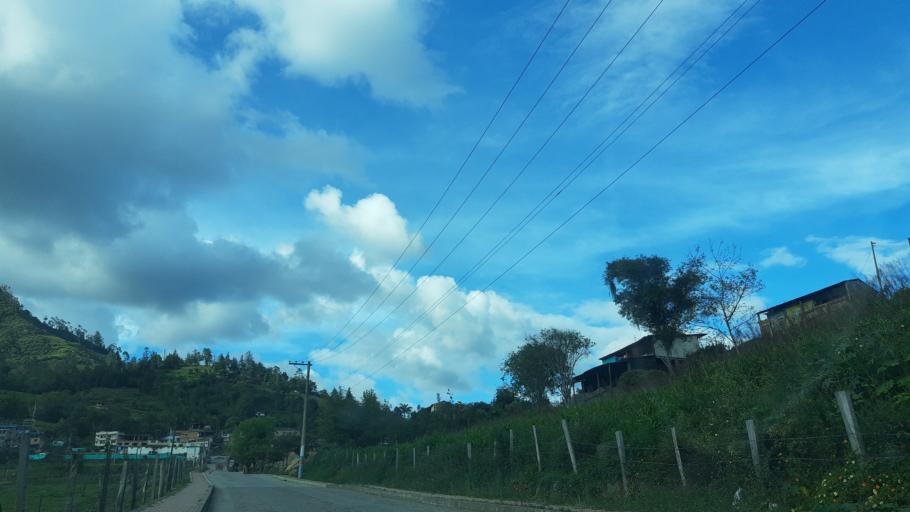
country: CO
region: Cundinamarca
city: Macheta
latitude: 5.0792
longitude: -73.6096
